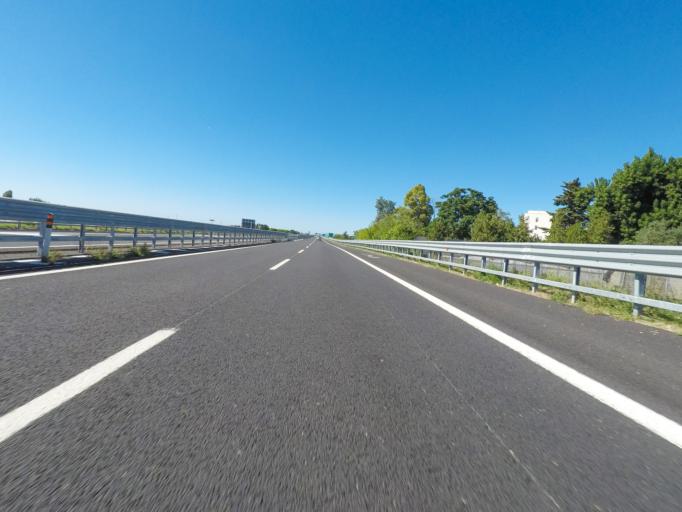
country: IT
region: Latium
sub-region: Provincia di Viterbo
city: Tarquinia
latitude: 42.2408
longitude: 11.7554
